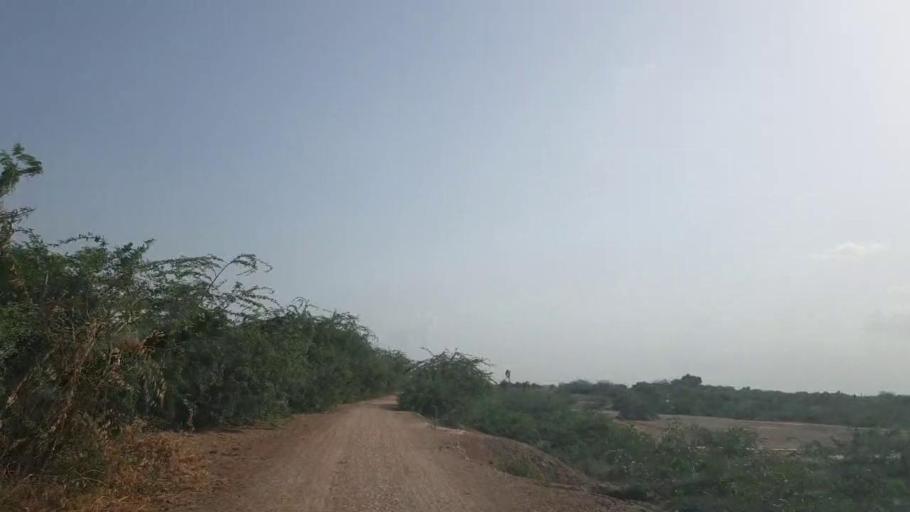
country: PK
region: Sindh
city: Tando Bago
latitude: 24.8025
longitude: 69.1852
